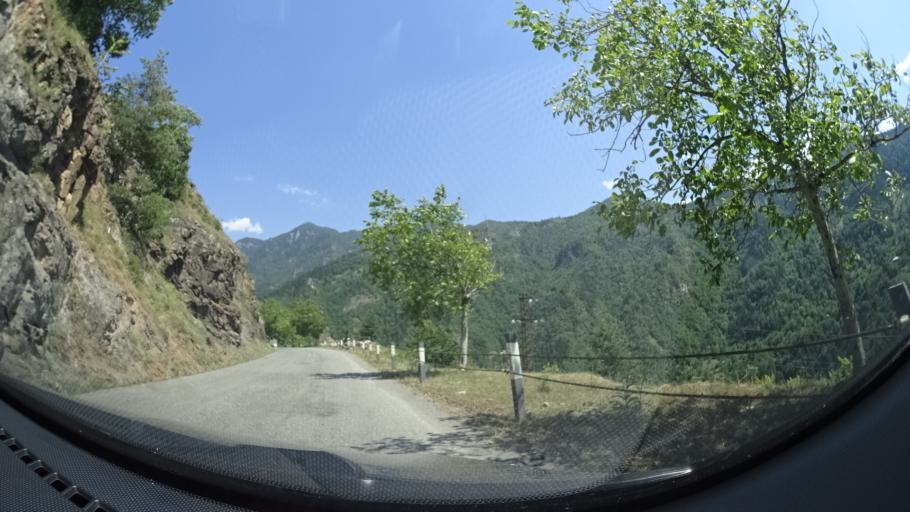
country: GE
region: Ajaria
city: Khulo
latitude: 41.6285
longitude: 42.2948
